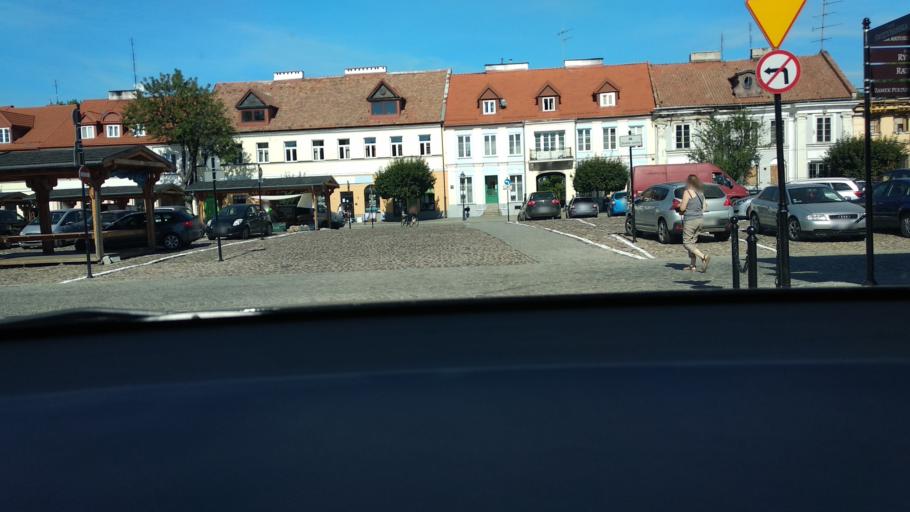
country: PL
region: Masovian Voivodeship
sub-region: Powiat pultuski
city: Pultusk
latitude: 52.7061
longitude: 21.0903
